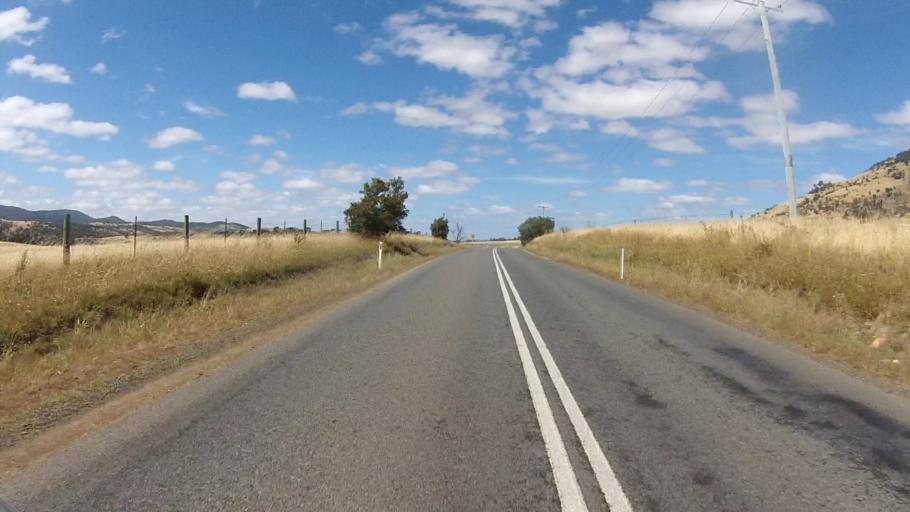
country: AU
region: Tasmania
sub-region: Sorell
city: Sorell
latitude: -42.6311
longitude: 147.4294
